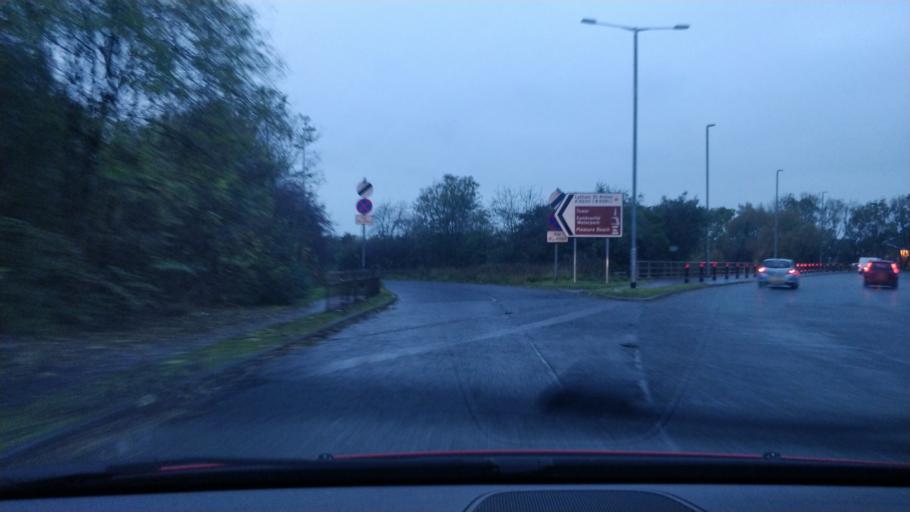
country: GB
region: England
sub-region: Lancashire
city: Poulton le Fylde
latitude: 53.7933
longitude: -2.9856
